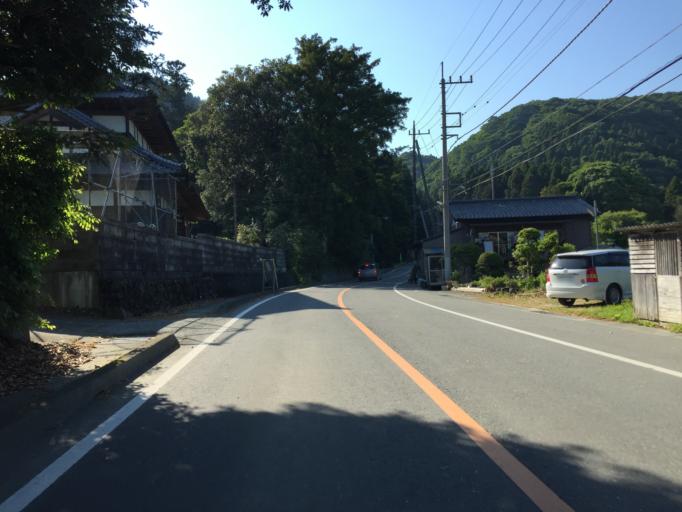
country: JP
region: Ibaraki
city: Kitaibaraki
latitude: 36.8596
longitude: 140.7236
